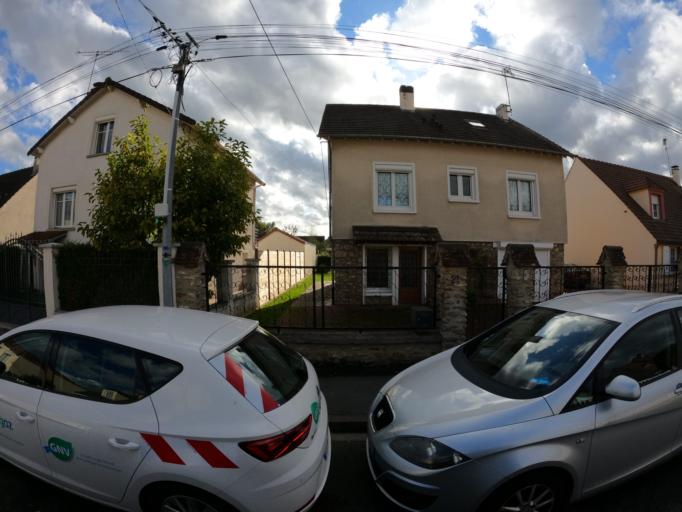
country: FR
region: Ile-de-France
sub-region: Departement de Seine-et-Marne
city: Esbly
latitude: 48.9014
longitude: 2.8097
